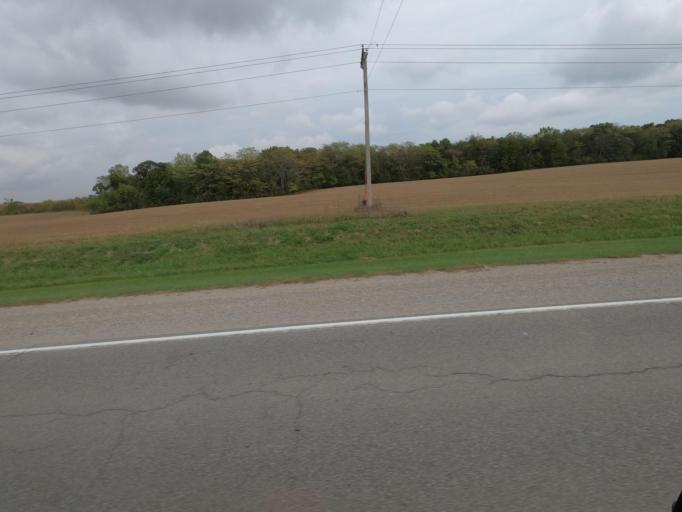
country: US
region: Iowa
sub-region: Wapello County
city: Ottumwa
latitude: 40.9413
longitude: -92.2270
